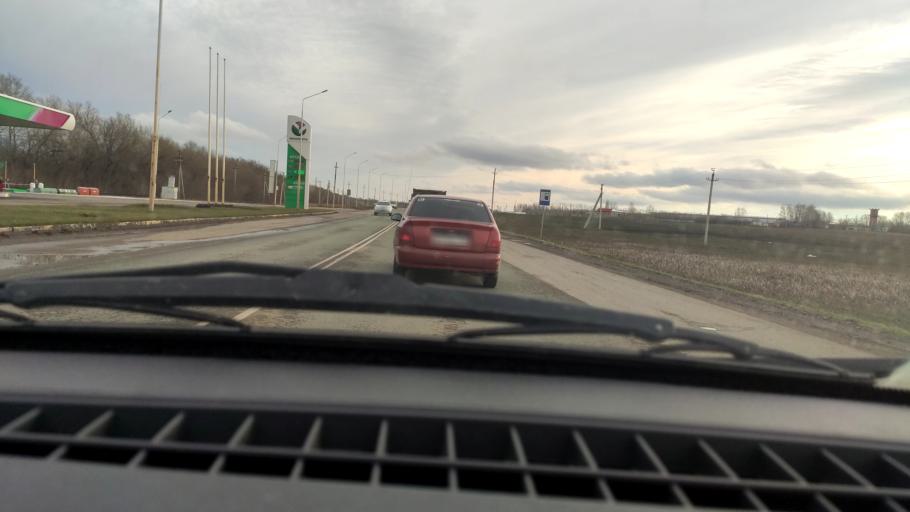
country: RU
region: Bashkortostan
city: Chishmy
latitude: 54.5727
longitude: 55.3562
